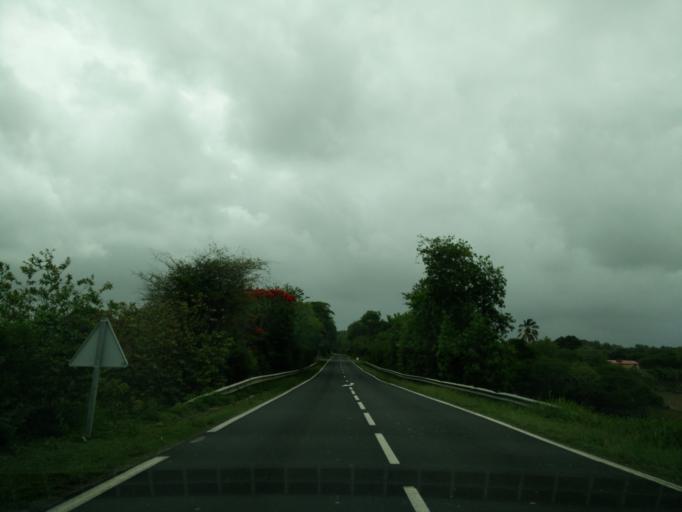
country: GP
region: Guadeloupe
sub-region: Guadeloupe
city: Grand-Bourg
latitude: 15.9075
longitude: -61.2695
